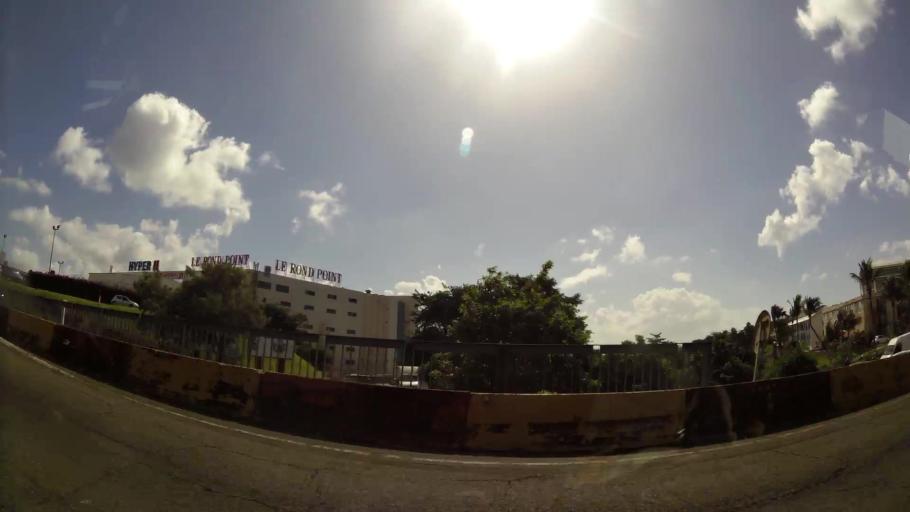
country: MQ
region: Martinique
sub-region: Martinique
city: Fort-de-France
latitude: 14.6053
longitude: -61.0893
